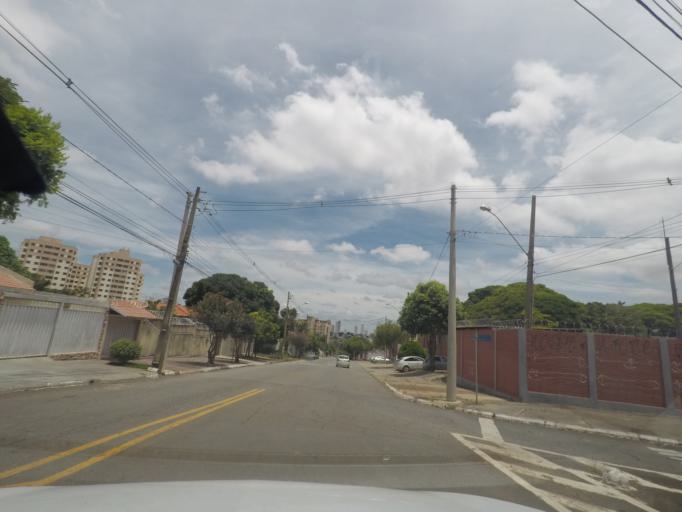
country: BR
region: Goias
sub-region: Goiania
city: Goiania
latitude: -16.6884
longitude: -49.2370
